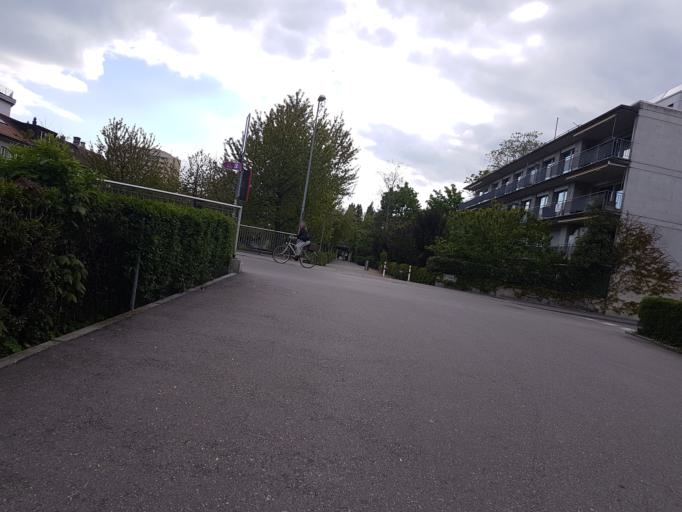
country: CH
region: Bern
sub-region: Biel/Bienne District
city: Biel/Bienne
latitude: 47.1348
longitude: 7.2407
